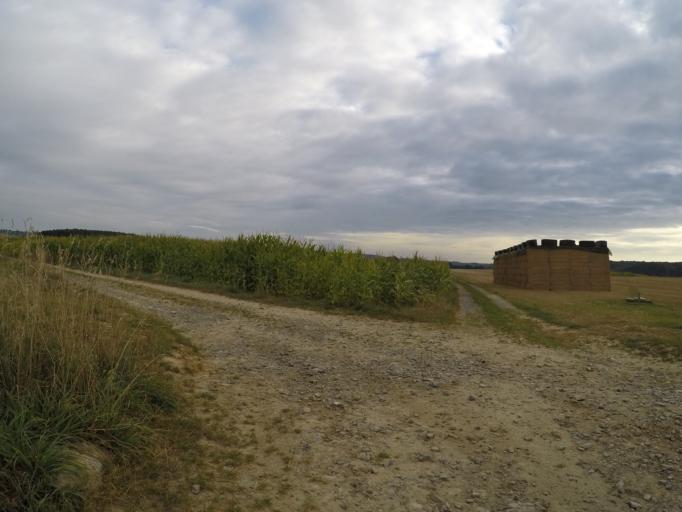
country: BE
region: Wallonia
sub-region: Province de Namur
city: Ciney
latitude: 50.3167
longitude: 5.0565
